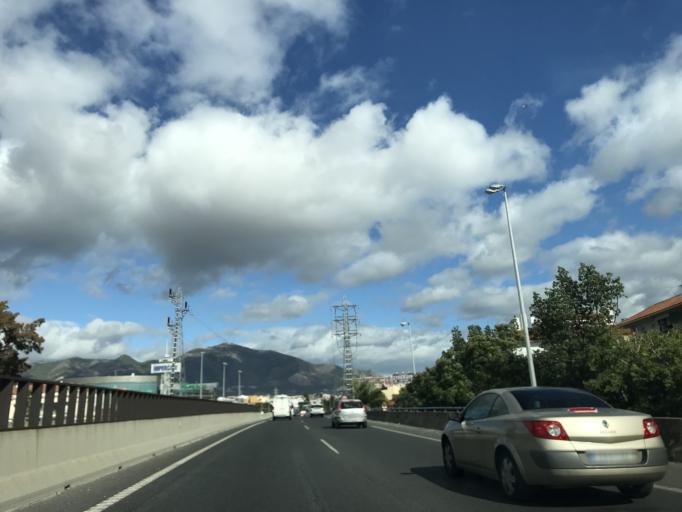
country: ES
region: Andalusia
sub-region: Provincia de Malaga
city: Fuengirola
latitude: 36.5448
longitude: -4.6335
